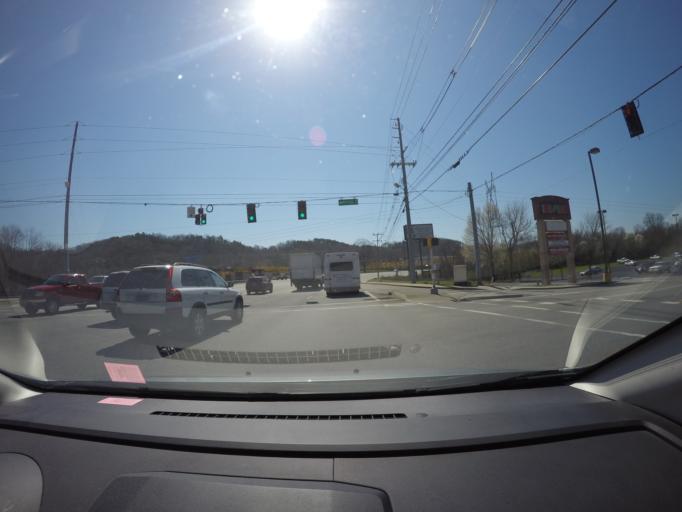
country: US
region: Tennessee
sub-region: Hamilton County
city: Signal Mountain
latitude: 35.0986
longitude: -85.3282
